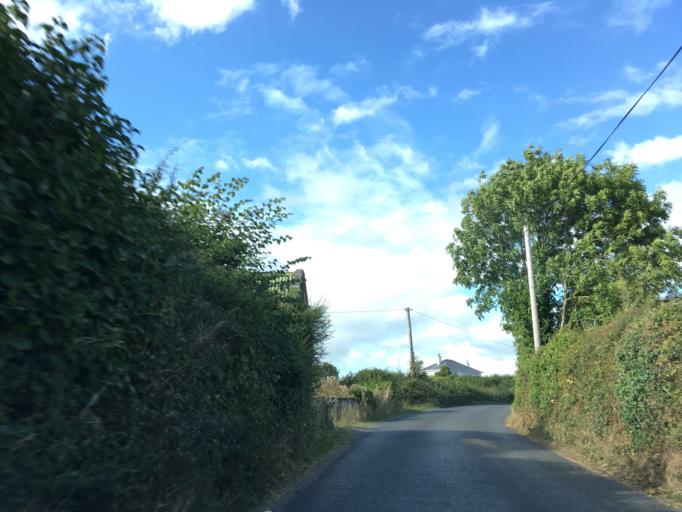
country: IE
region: Munster
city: Cahir
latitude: 52.2878
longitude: -7.9549
